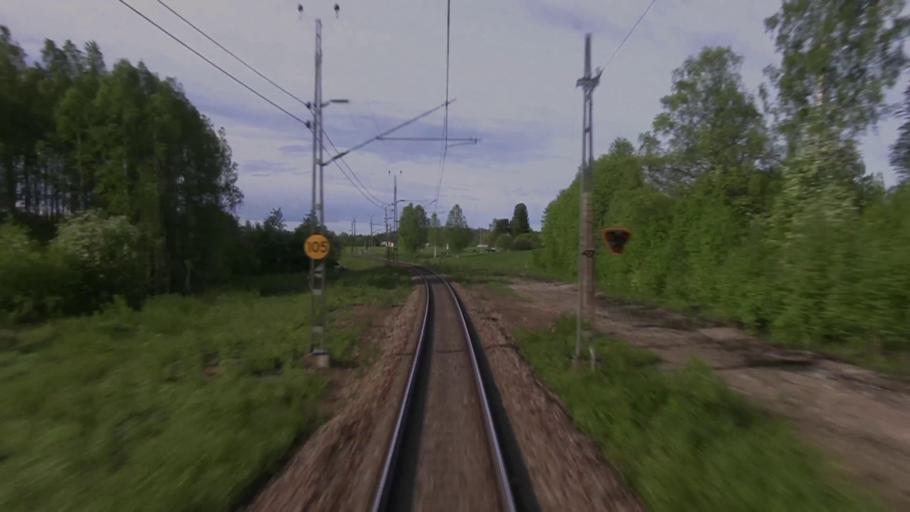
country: SE
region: Vaesterbotten
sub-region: Vindelns Kommun
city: Vindeln
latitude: 64.0969
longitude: 19.6744
